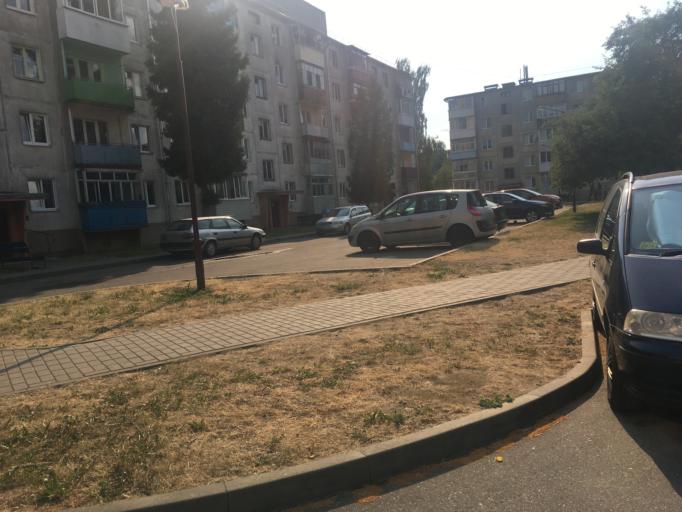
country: BY
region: Grodnenskaya
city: Hrodna
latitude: 53.6684
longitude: 23.8038
